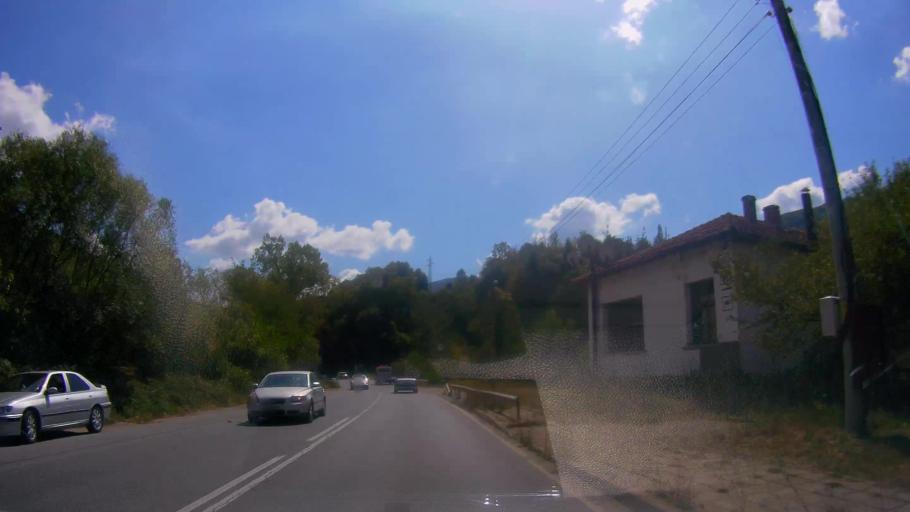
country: BG
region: Stara Zagora
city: Gurkovo
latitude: 42.7198
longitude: 25.7149
